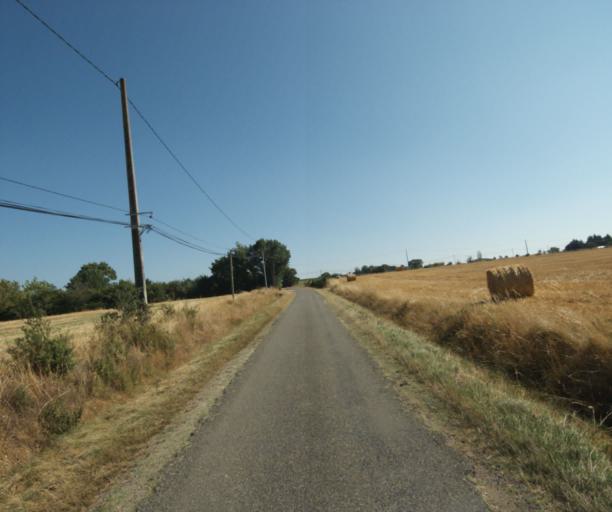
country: FR
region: Midi-Pyrenees
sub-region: Departement de la Haute-Garonne
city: Saint-Felix-Lauragais
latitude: 43.4928
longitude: 1.9237
